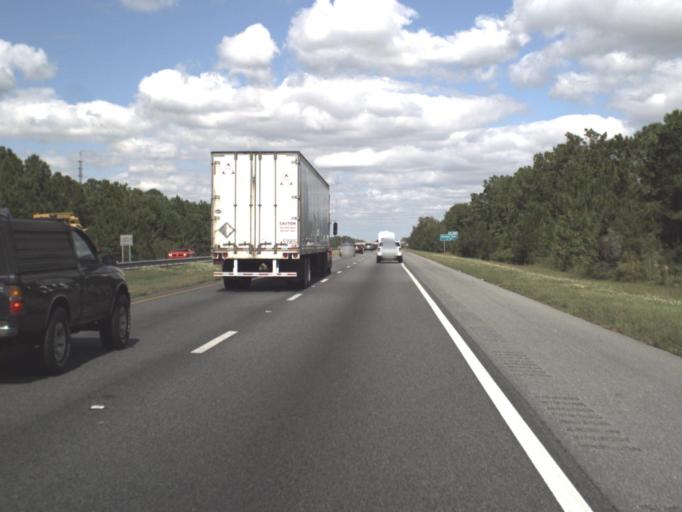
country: US
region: Florida
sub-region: Osceola County
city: Buenaventura Lakes
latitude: 28.3280
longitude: -81.3750
